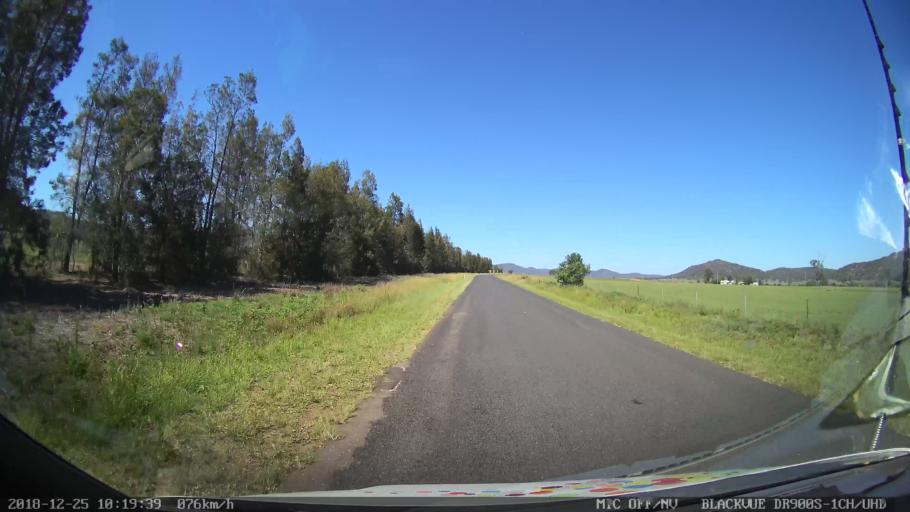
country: AU
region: New South Wales
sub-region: Muswellbrook
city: Denman
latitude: -32.3527
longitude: 150.5570
